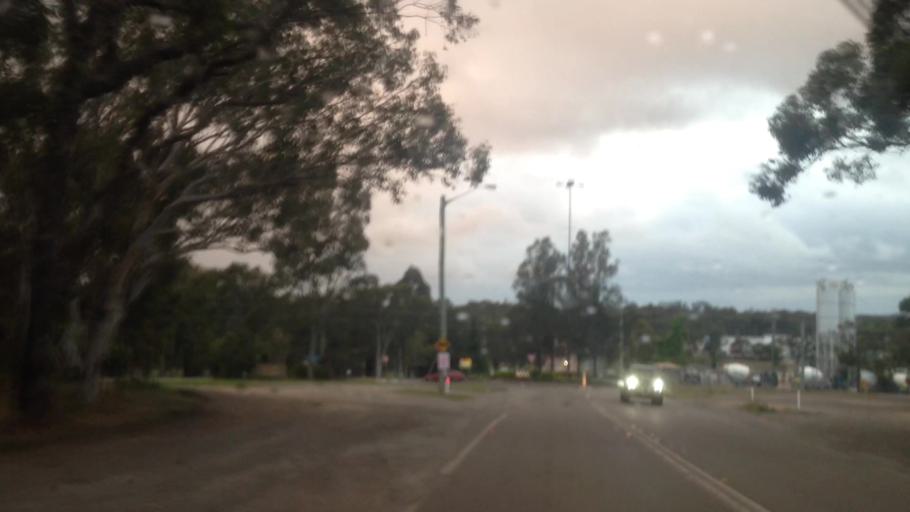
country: AU
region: New South Wales
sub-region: Lake Macquarie Shire
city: Dora Creek
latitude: -33.1118
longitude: 151.4782
